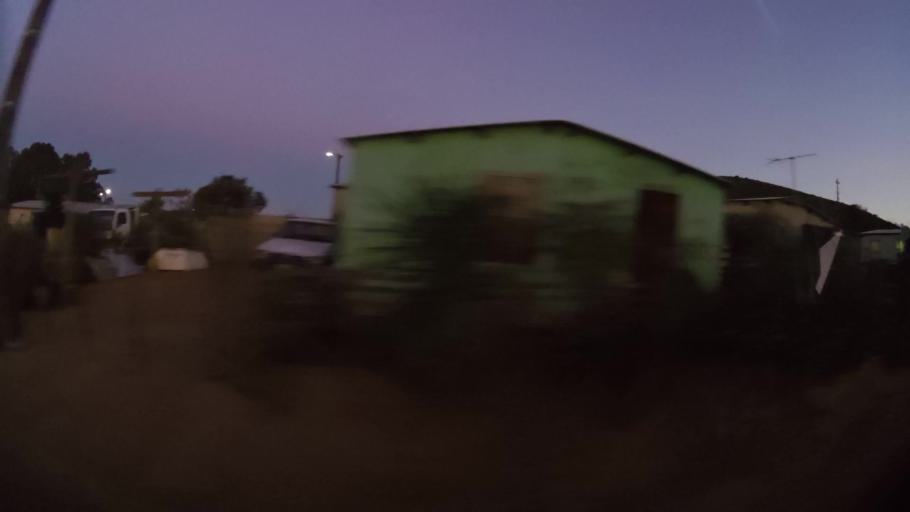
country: ZA
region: Western Cape
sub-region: Eden District Municipality
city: Riversdale
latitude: -34.1064
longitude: 21.2746
